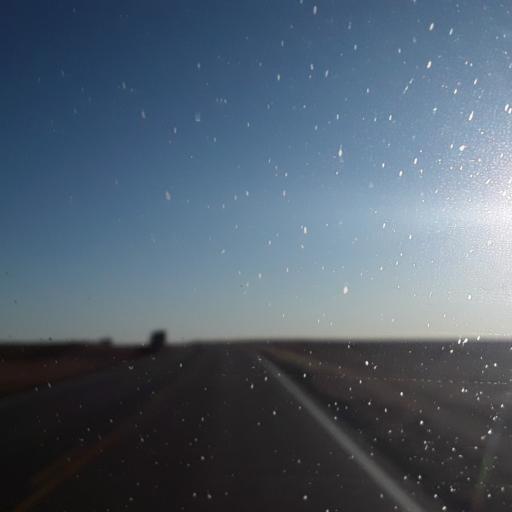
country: US
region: Kansas
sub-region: Wallace County
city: Sharon Springs
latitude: 39.1004
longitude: -101.7365
